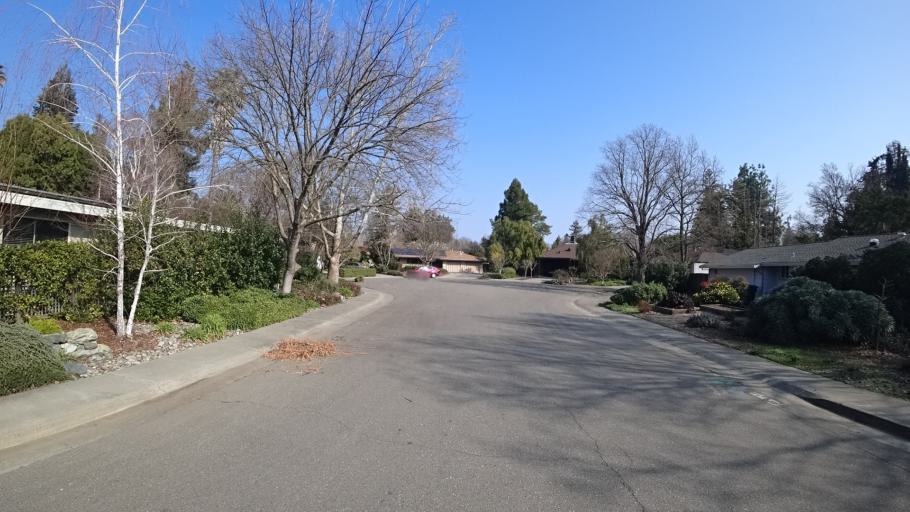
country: US
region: California
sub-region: Yolo County
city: Davis
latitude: 38.5486
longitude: -121.7741
